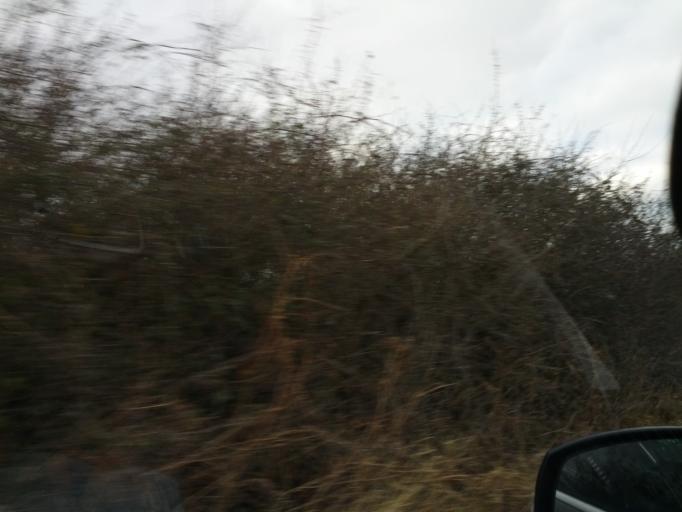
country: IE
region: Connaught
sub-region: County Galway
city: Gort
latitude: 53.1616
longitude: -8.8512
